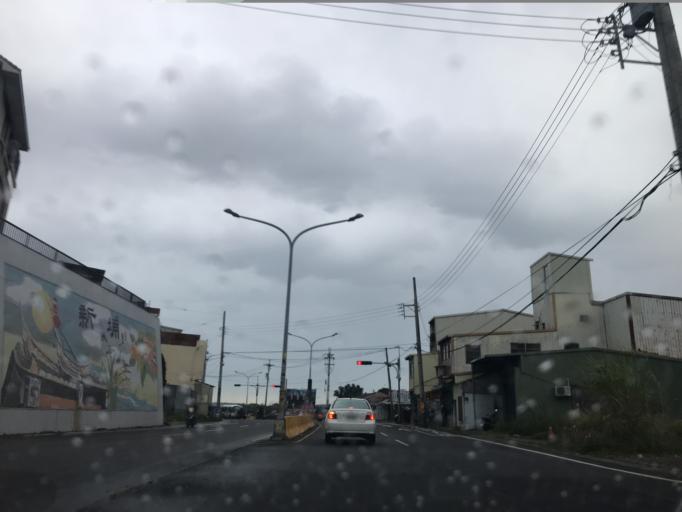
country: TW
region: Taiwan
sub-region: Hsinchu
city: Zhubei
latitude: 24.8292
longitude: 121.0434
